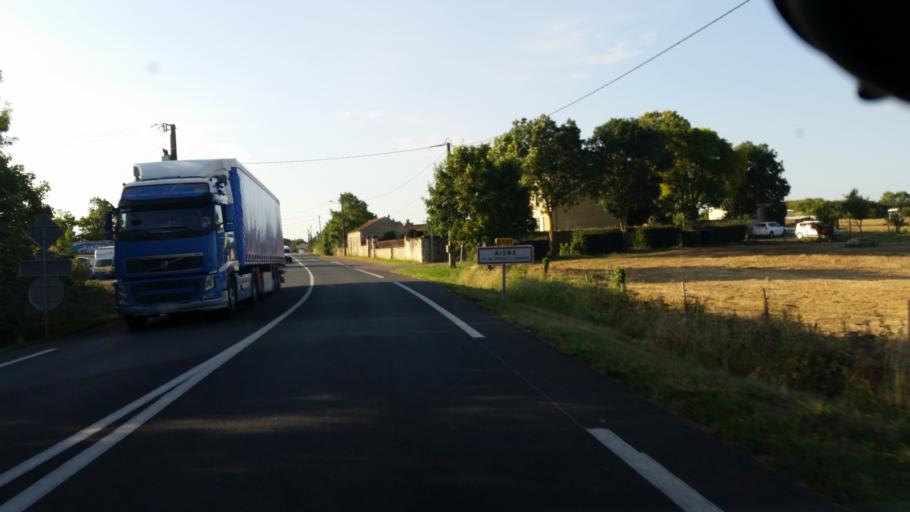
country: FR
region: Pays de la Loire
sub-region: Departement de la Vendee
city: Chaille-les-Marais
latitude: 46.3842
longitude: -1.0252
